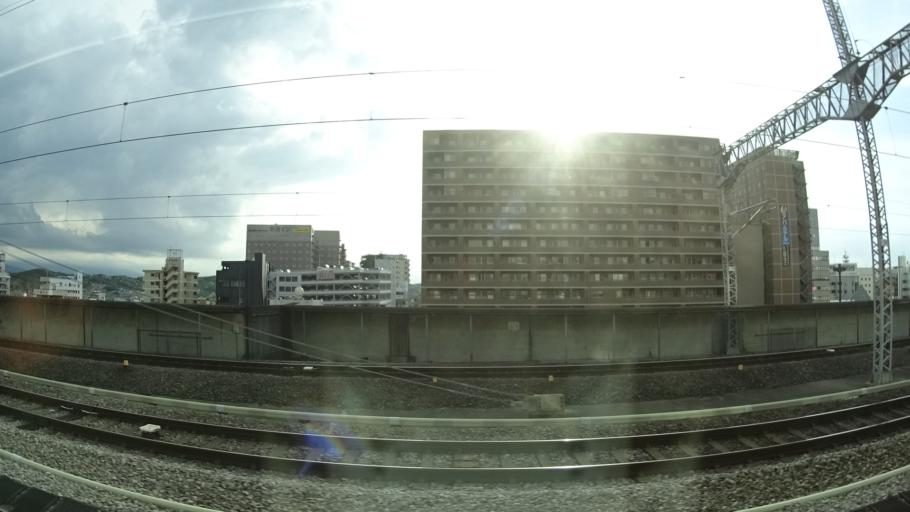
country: JP
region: Gunma
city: Takasaki
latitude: 36.3215
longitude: 139.0131
